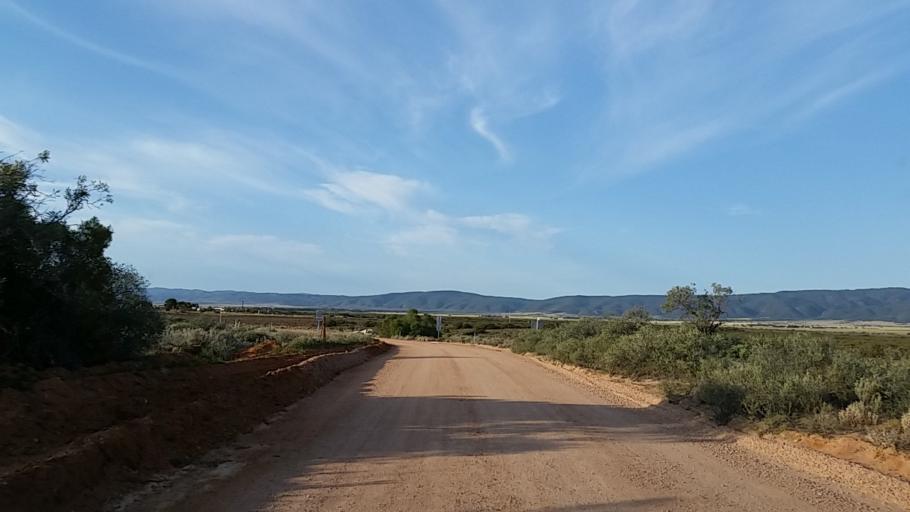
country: AU
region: South Australia
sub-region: Port Pirie City and Dists
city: Port Pirie
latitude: -33.1058
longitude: 138.0333
